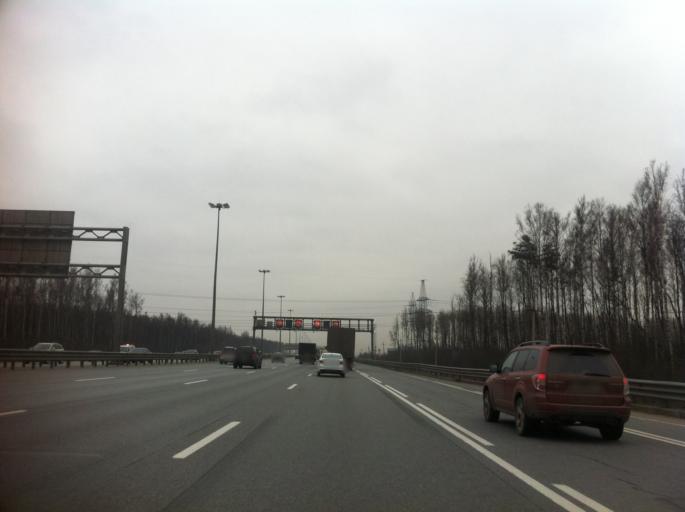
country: RU
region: Leningrad
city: Rybatskoye
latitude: 59.8860
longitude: 30.5250
